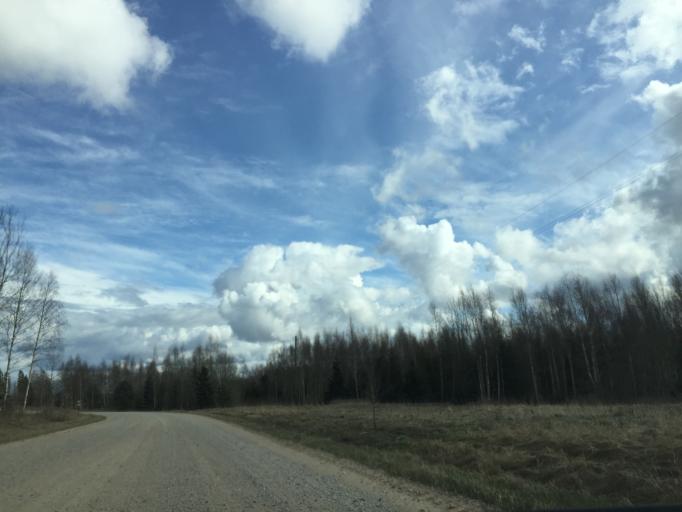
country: LV
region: Limbazu Rajons
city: Limbazi
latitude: 57.6034
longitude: 24.8006
